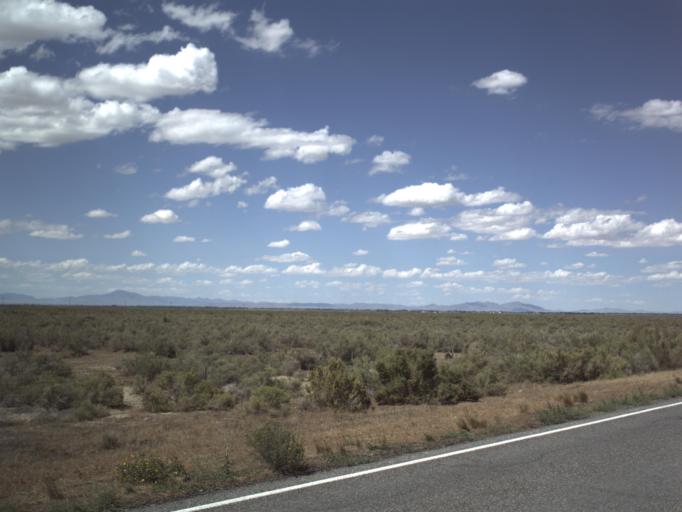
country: US
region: Utah
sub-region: Millard County
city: Delta
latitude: 39.2421
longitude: -112.4341
